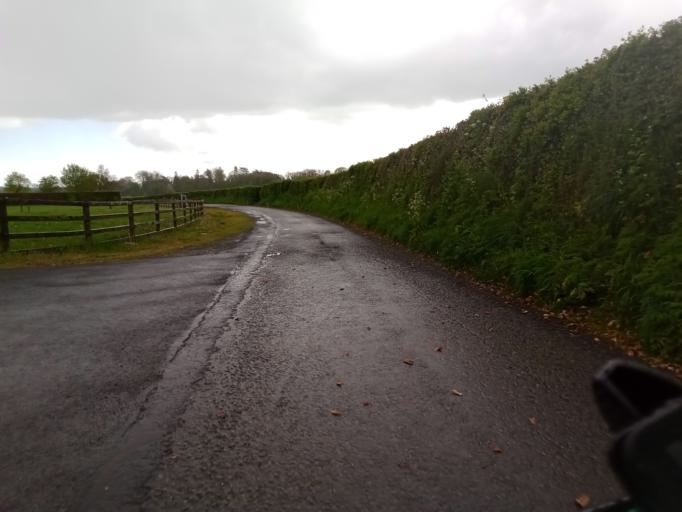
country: IE
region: Leinster
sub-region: Kilkenny
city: Kilkenny
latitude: 52.6820
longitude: -7.2680
